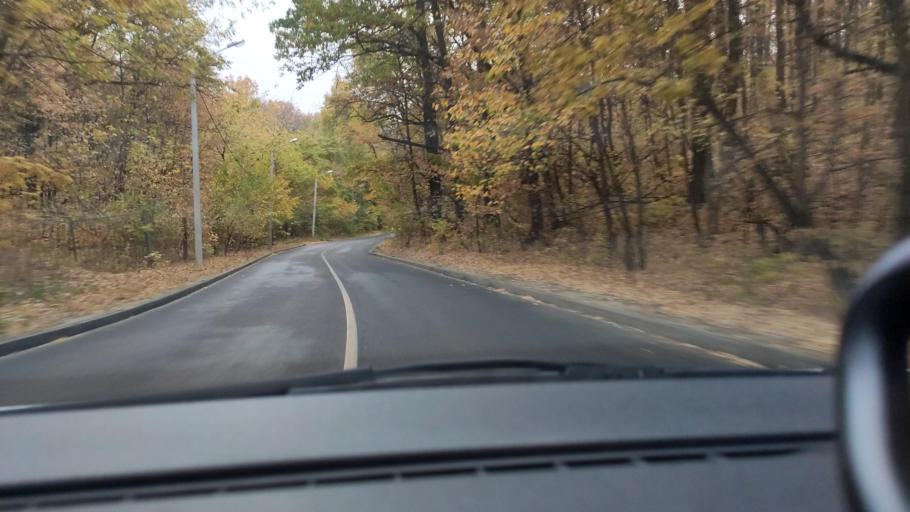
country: RU
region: Voronezj
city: Voronezh
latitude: 51.7194
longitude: 39.2351
